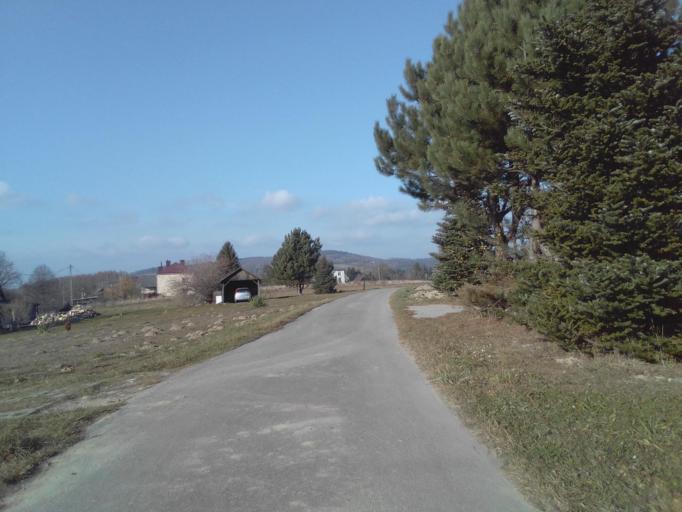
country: PL
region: Subcarpathian Voivodeship
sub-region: Powiat strzyzowski
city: Gwoznica Gorna
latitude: 49.8313
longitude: 21.9752
